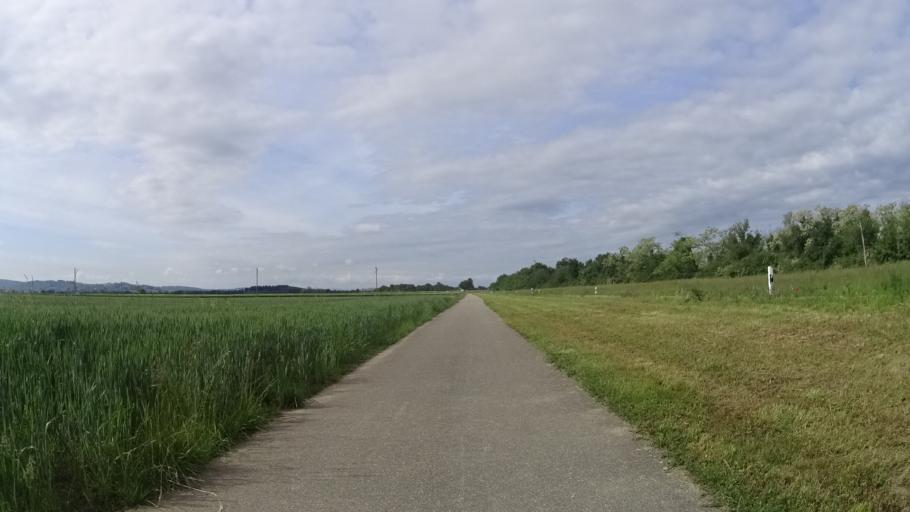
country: DE
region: Baden-Wuerttemberg
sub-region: Freiburg Region
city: Neuenburg am Rhein
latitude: 47.8001
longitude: 7.5600
